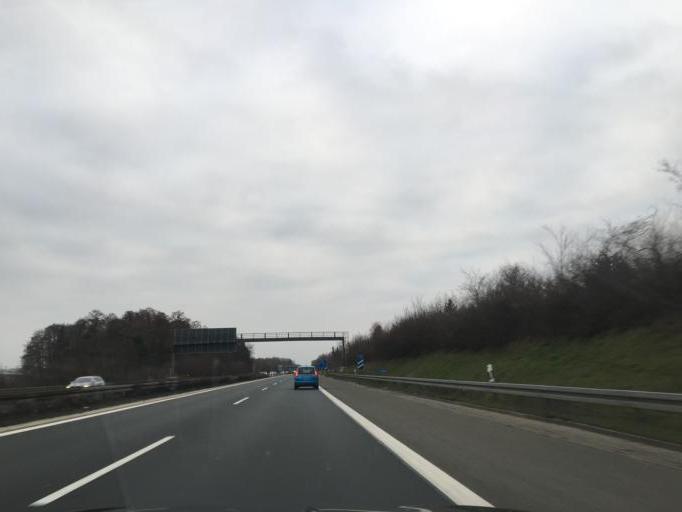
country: DE
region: Bavaria
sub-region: Regierungsbezirk Mittelfranken
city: Erlangen
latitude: 49.5477
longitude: 10.9930
